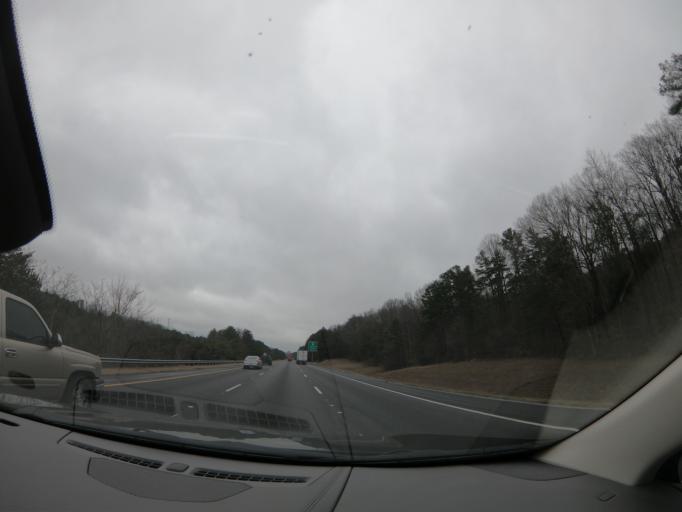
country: US
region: Georgia
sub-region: Whitfield County
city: Varnell
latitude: 34.8445
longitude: -85.0173
